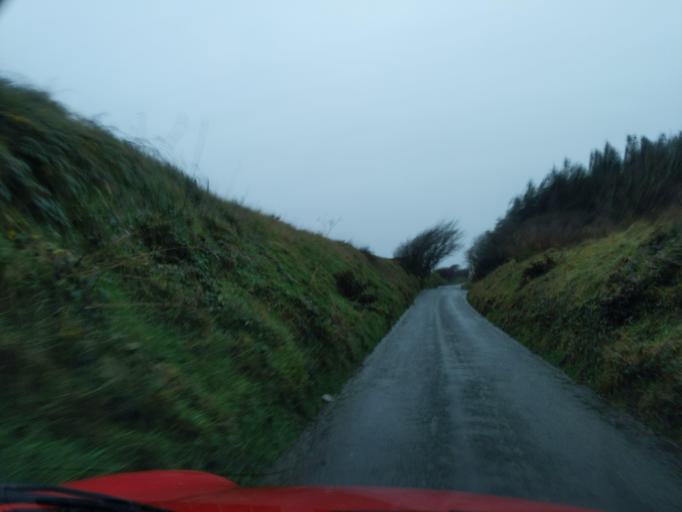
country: GB
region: England
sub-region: Cornwall
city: Camelford
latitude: 50.6488
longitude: -4.6999
